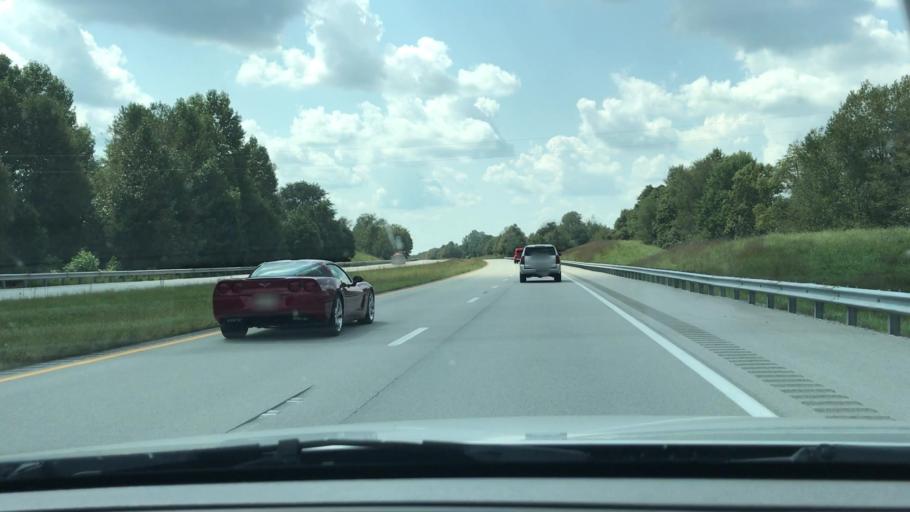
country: US
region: Kentucky
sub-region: Russell County
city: Russell Springs
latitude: 37.0989
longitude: -84.8666
